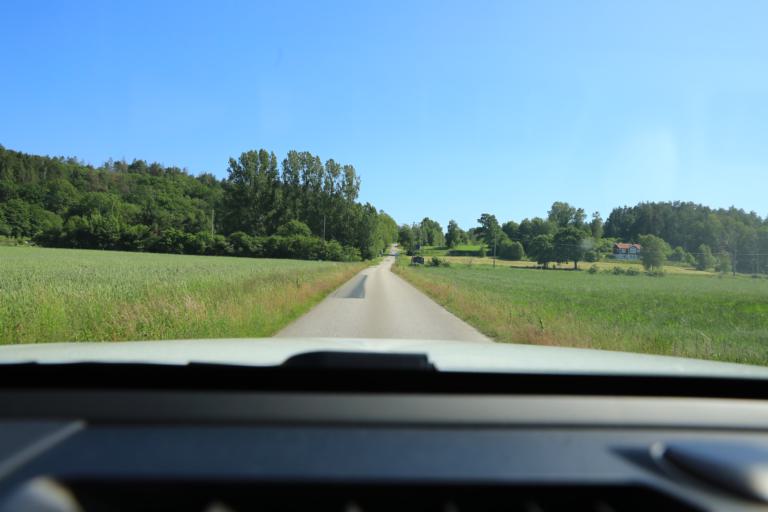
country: SE
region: Halland
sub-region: Varbergs Kommun
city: Veddige
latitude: 57.1998
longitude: 12.3203
